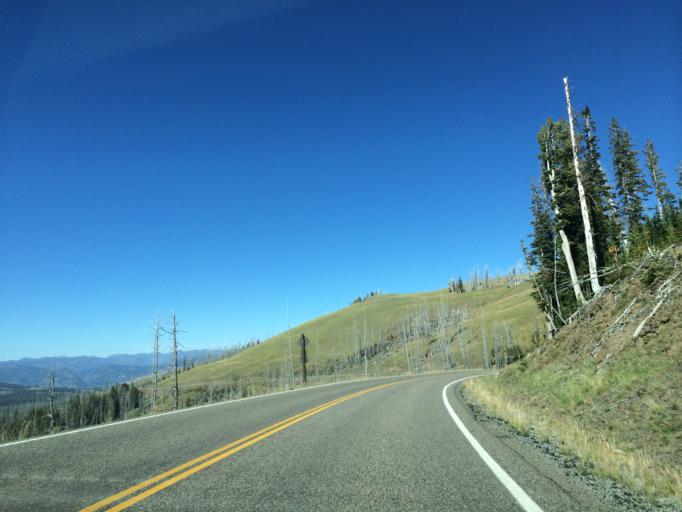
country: US
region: Montana
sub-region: Gallatin County
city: West Yellowstone
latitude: 44.8177
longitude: -110.4500
